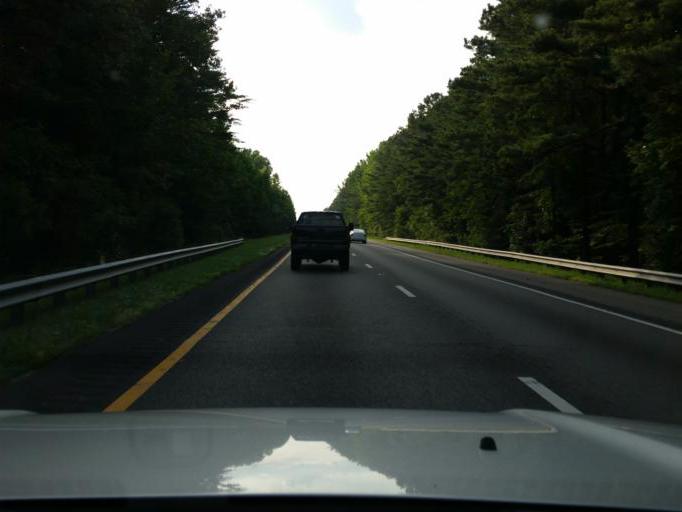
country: US
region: Virginia
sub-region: King William County
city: West Point
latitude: 37.4538
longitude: -76.8713
